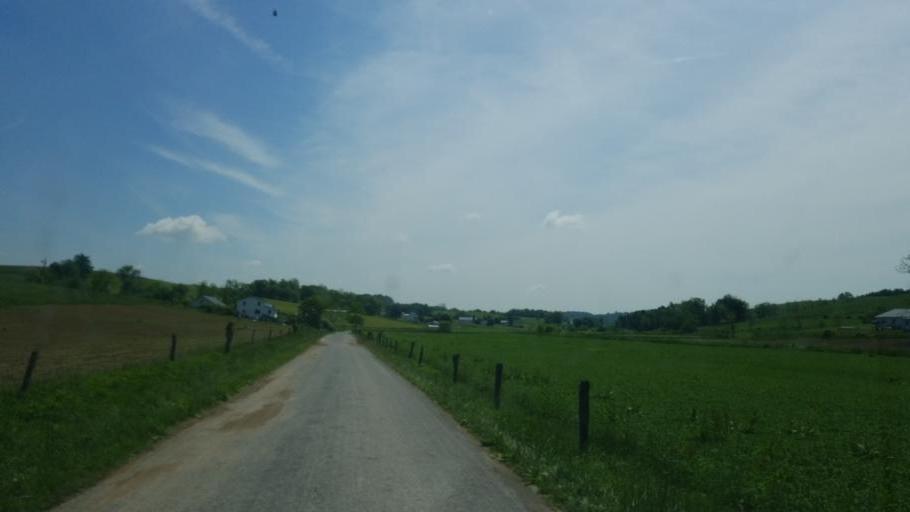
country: US
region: Ohio
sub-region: Tuscarawas County
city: Sugarcreek
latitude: 40.5561
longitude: -81.7466
